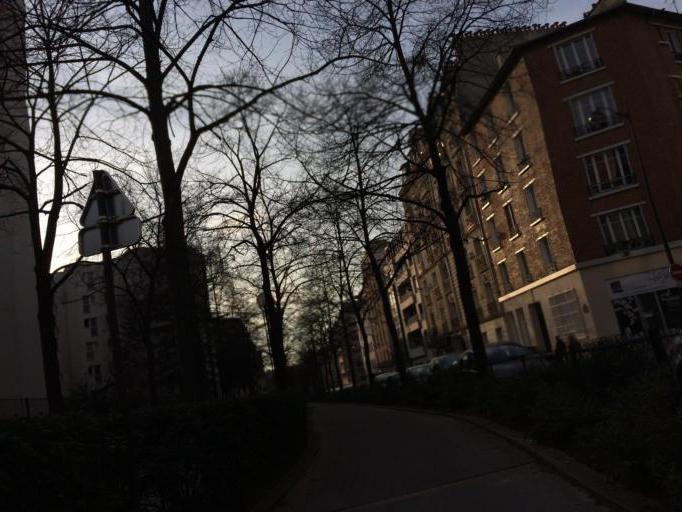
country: FR
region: Ile-de-France
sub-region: Departement du Val-de-Marne
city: Saint-Mande
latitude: 48.8406
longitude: 2.4076
